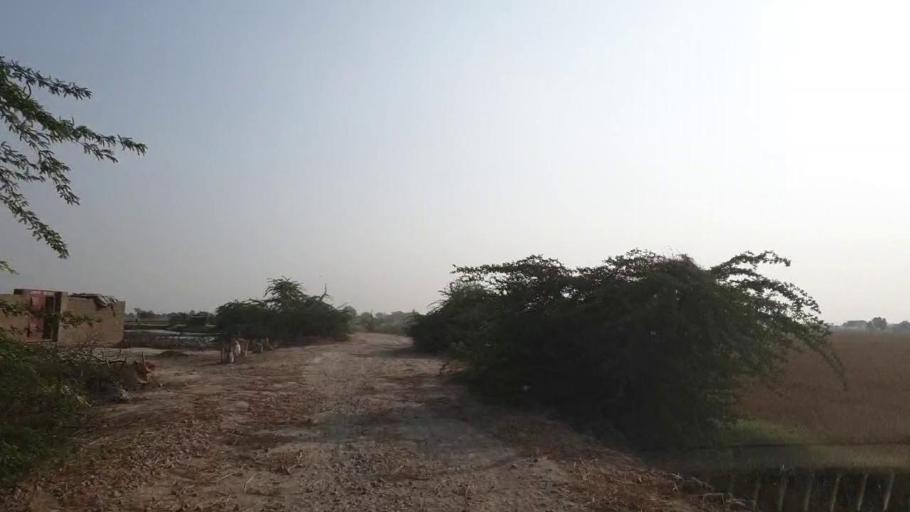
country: PK
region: Sindh
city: Kario
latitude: 24.9050
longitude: 68.5679
